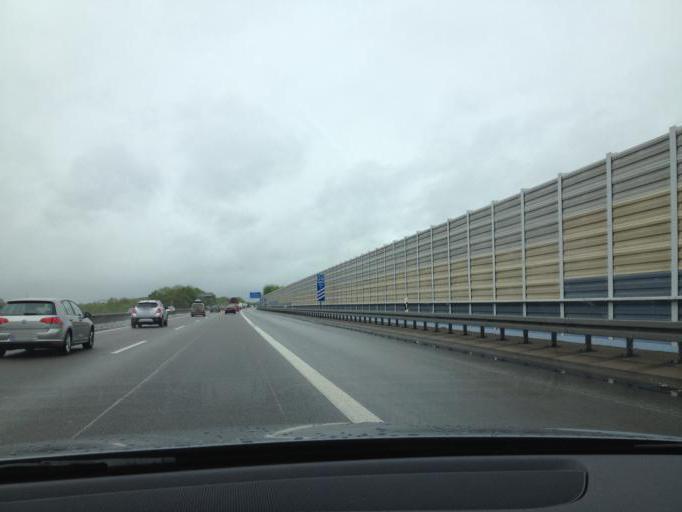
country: DE
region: Baden-Wuerttemberg
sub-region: Regierungsbezirk Stuttgart
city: Neckarsulm
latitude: 49.1853
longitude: 9.2058
